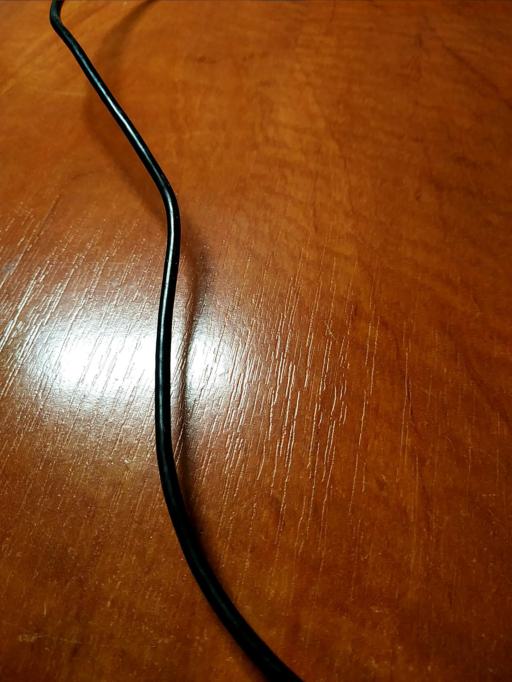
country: BY
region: Mogilev
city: Khotsimsk
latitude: 53.5439
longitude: 32.5066
